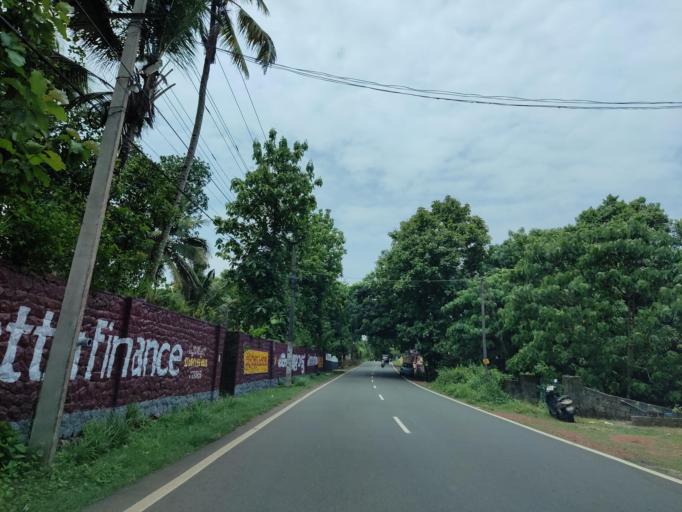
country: IN
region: Kerala
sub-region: Alappuzha
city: Chengannur
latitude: 9.2938
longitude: 76.6221
